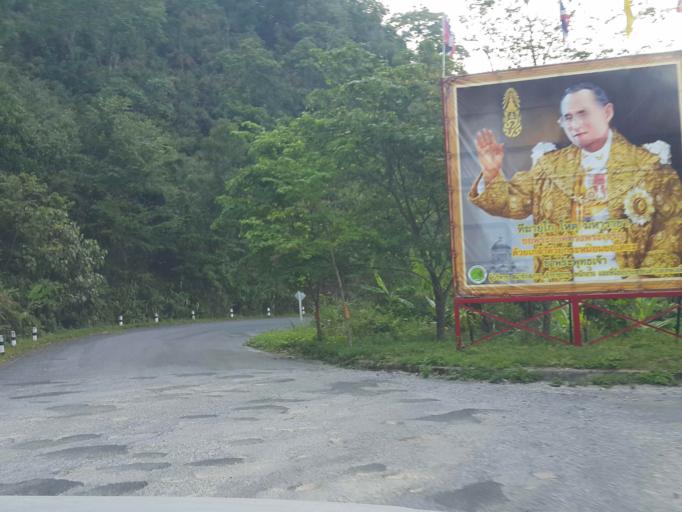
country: TH
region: Chiang Mai
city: Mae On
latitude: 18.9424
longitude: 99.3568
